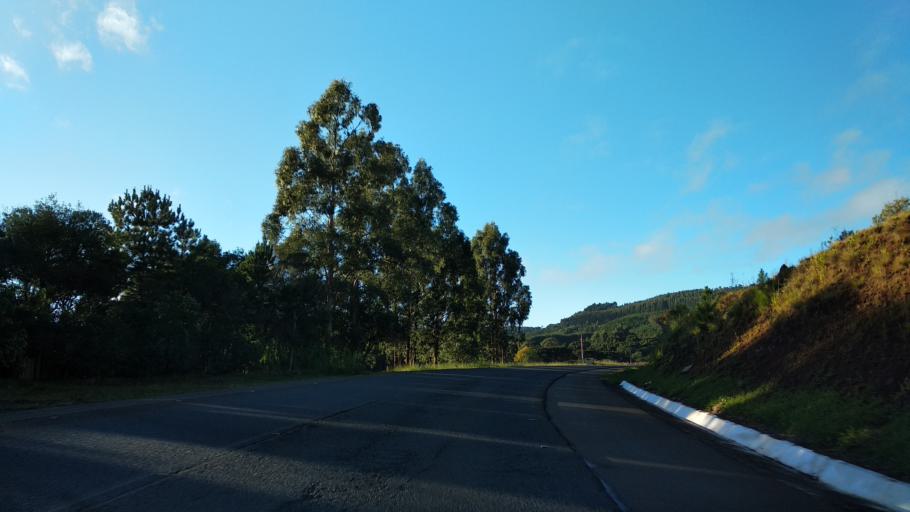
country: BR
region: Santa Catarina
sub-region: Curitibanos
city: Curitibanos
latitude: -27.5962
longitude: -50.7315
